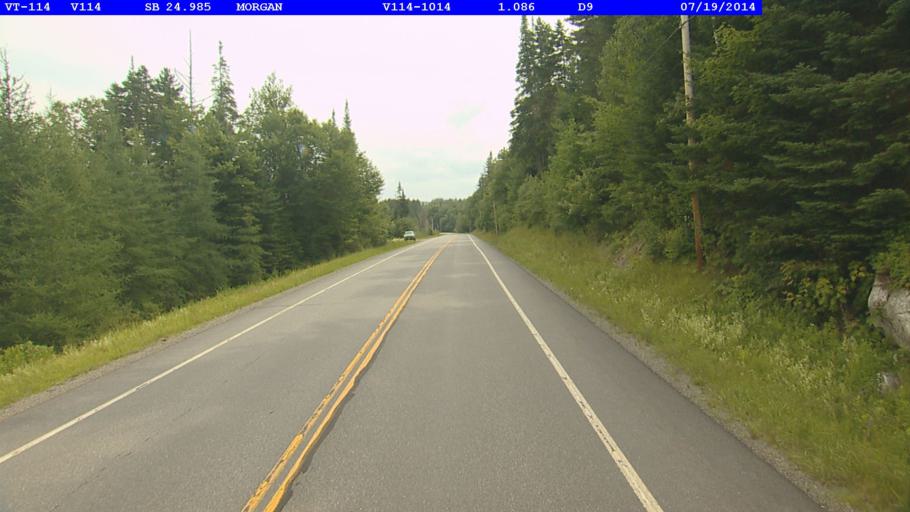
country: CA
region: Quebec
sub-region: Estrie
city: Coaticook
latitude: 44.8622
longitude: -71.9088
